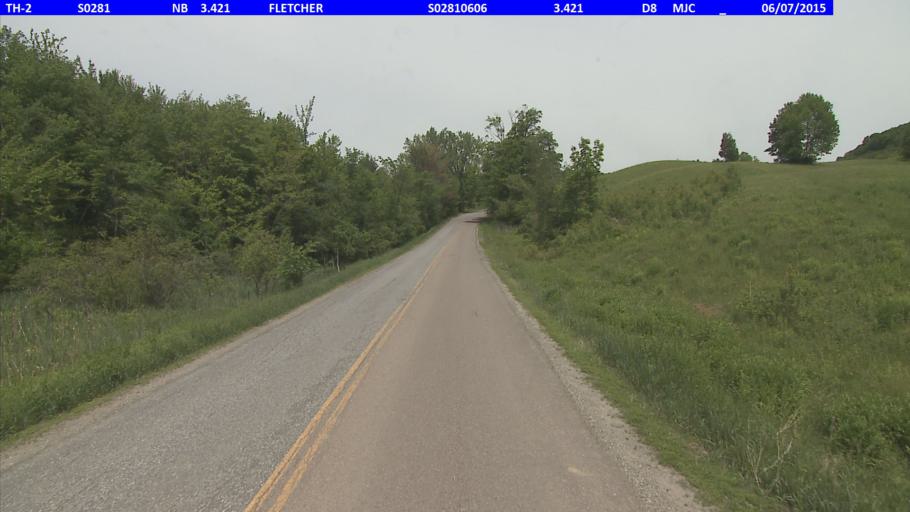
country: US
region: Vermont
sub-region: Franklin County
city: Saint Albans
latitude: 44.7165
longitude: -72.9546
